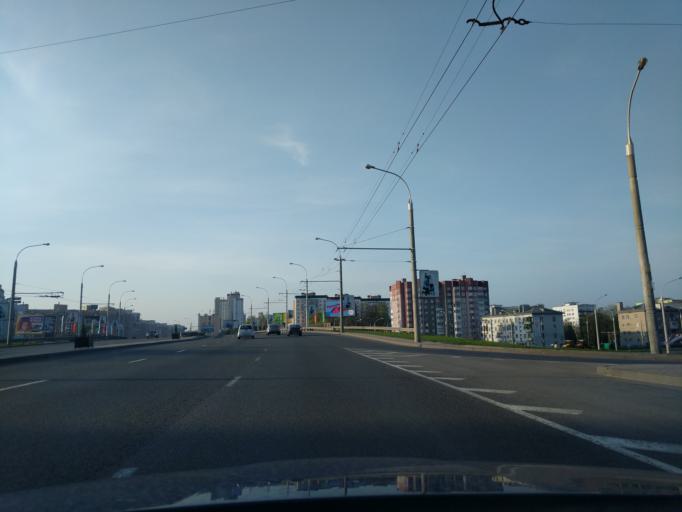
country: BY
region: Minsk
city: Minsk
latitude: 53.8713
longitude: 27.5705
